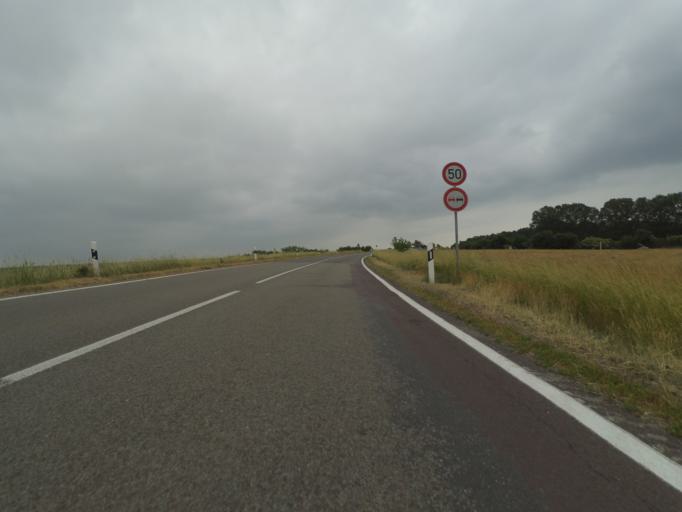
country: DE
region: Mecklenburg-Vorpommern
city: Neustadt-Glewe
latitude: 53.3710
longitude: 11.6563
